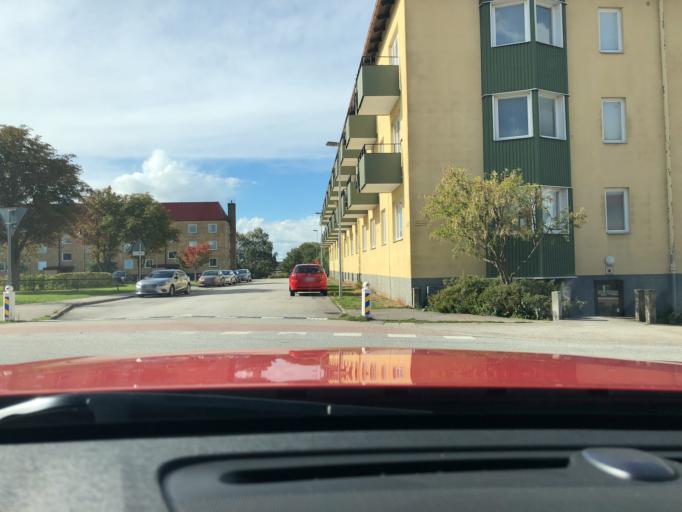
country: SE
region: Skane
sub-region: Sjobo Kommun
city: Sjoebo
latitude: 55.6353
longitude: 13.7042
